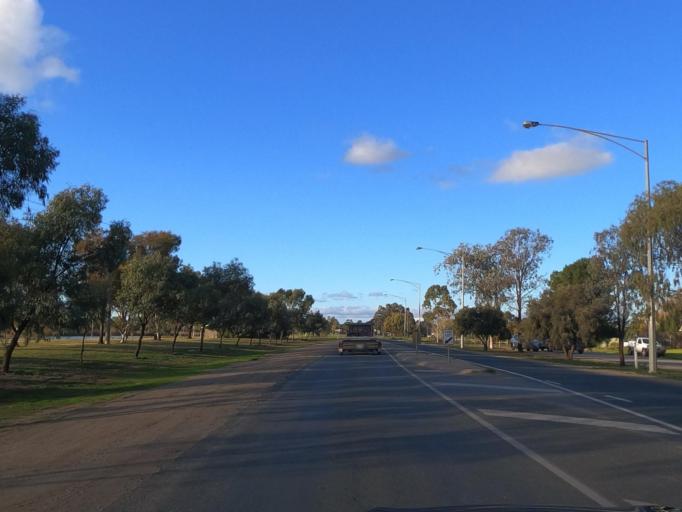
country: AU
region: Victoria
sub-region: Swan Hill
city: Swan Hill
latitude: -35.3413
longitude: 143.5362
